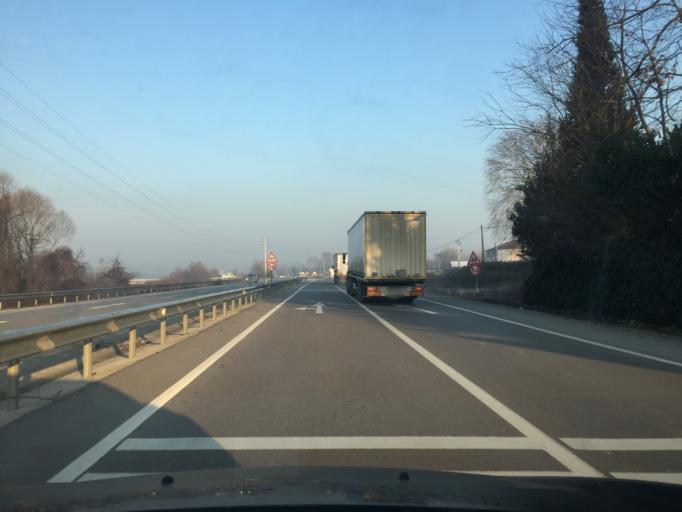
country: TR
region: Sakarya
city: Akyazi
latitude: 40.6711
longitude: 30.5881
